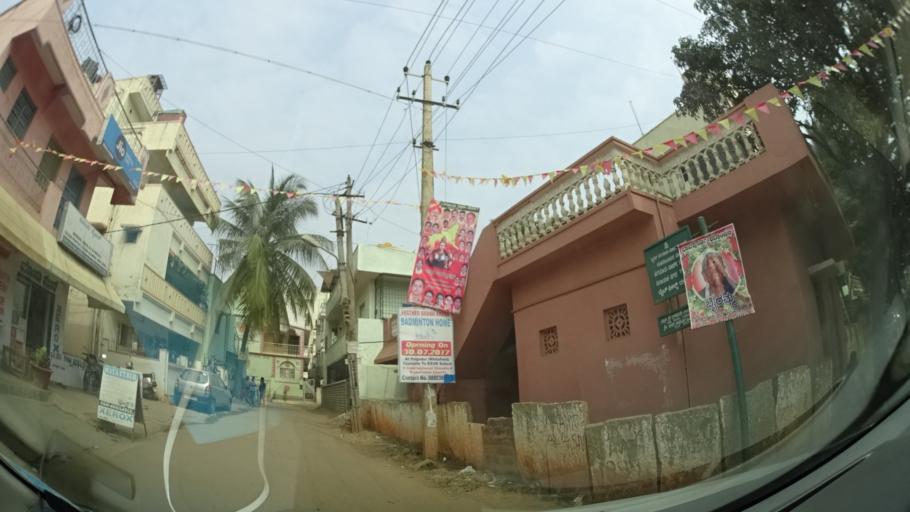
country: IN
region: Karnataka
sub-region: Bangalore Rural
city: Hoskote
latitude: 12.9644
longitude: 77.7540
